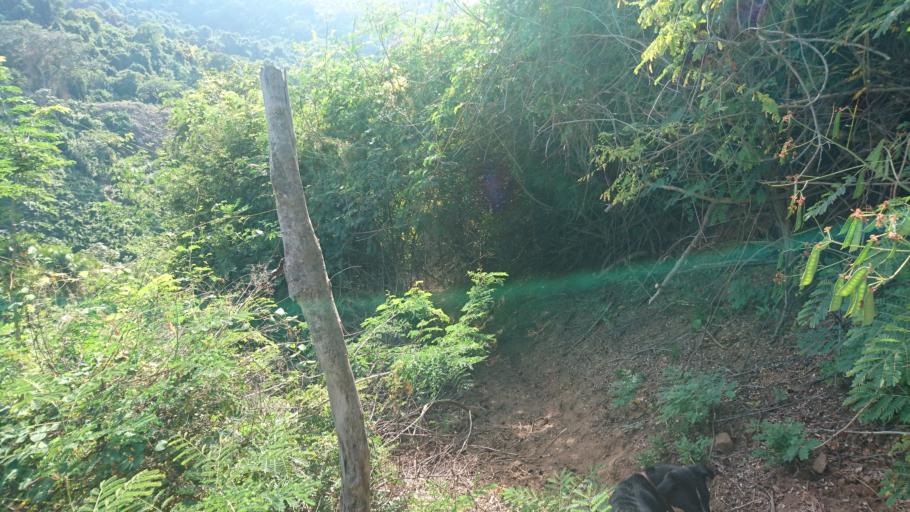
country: MX
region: Nayarit
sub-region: Bahia de Banderas
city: Corral del Risco (Punta de Mita)
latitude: 20.8301
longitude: -105.4653
